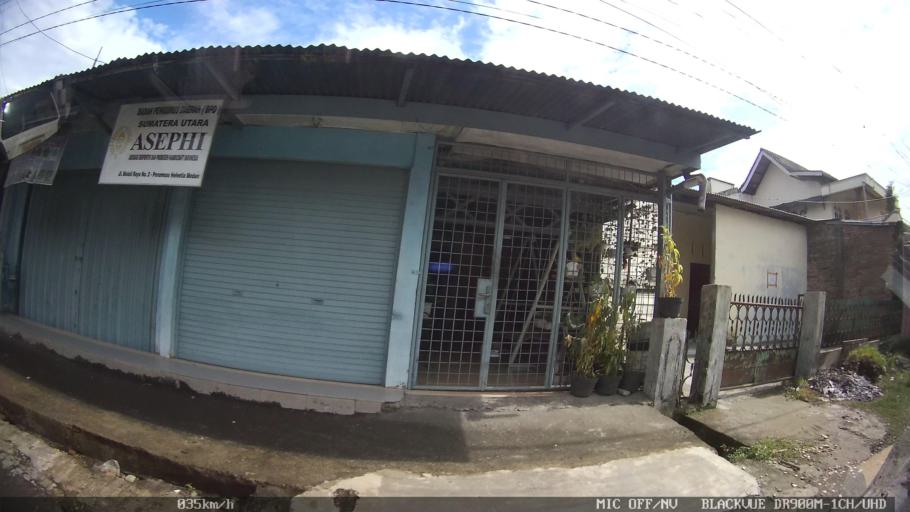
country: ID
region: North Sumatra
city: Sunggal
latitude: 3.6139
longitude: 98.6307
